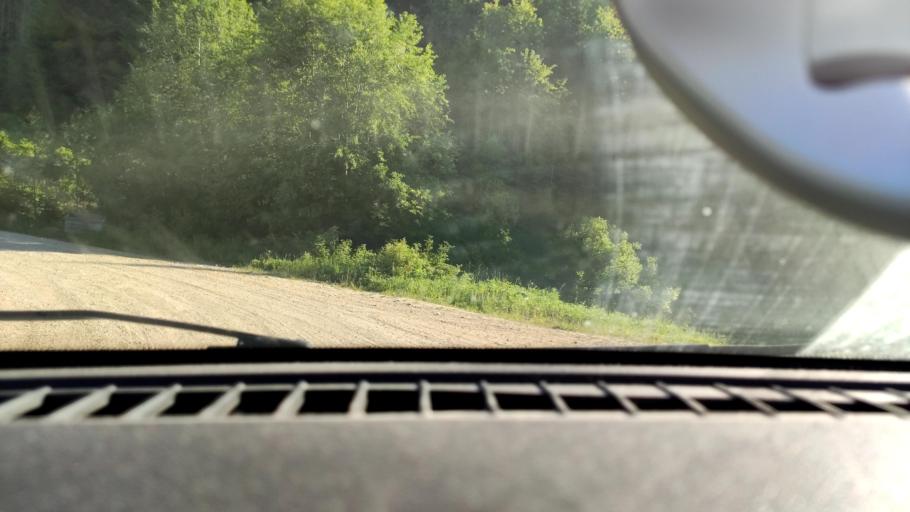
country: RU
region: Perm
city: Novyye Lyady
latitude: 58.1777
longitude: 56.5694
